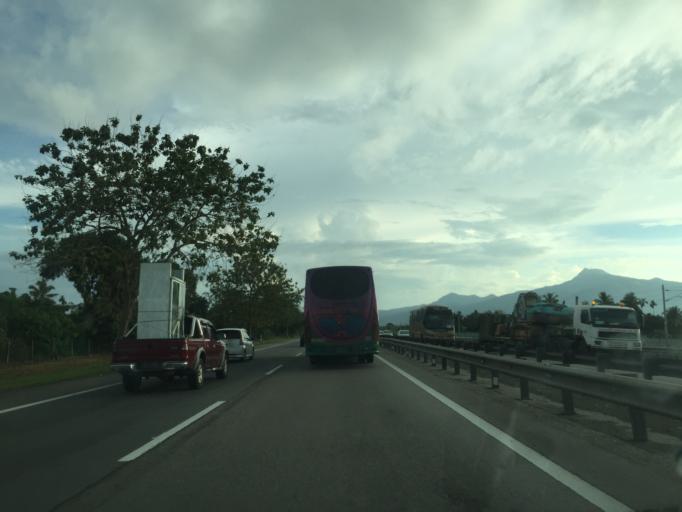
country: MY
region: Kedah
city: Gurun
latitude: 5.8885
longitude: 100.4774
